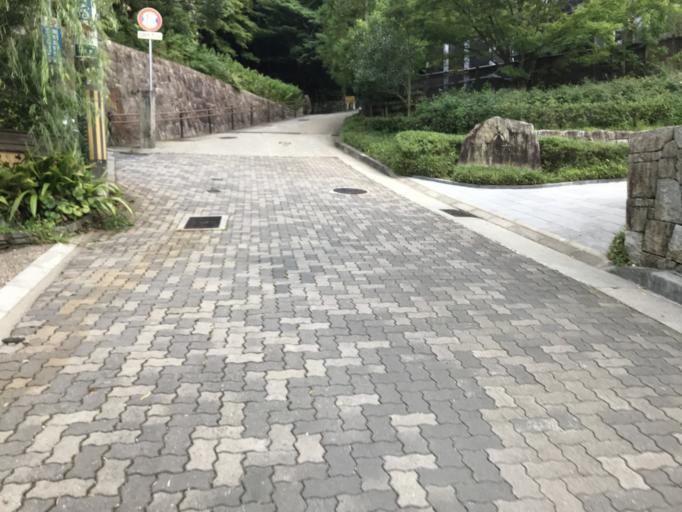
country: JP
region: Hyogo
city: Ashiya
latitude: 34.7951
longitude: 135.2500
